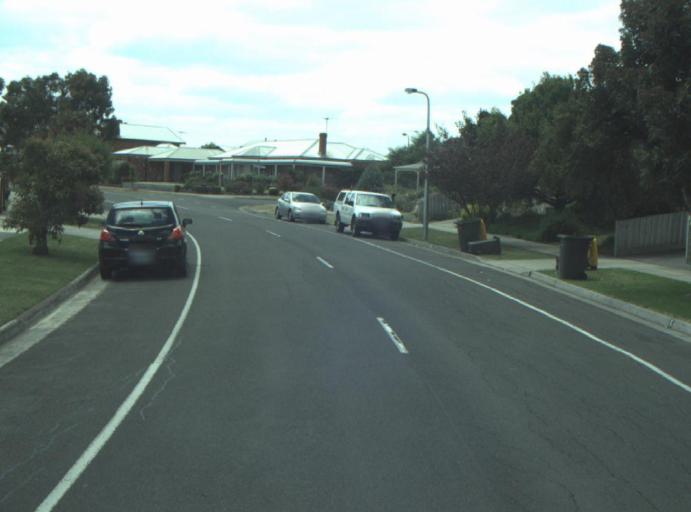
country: AU
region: Victoria
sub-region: Greater Geelong
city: Wandana Heights
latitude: -38.1924
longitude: 144.3217
